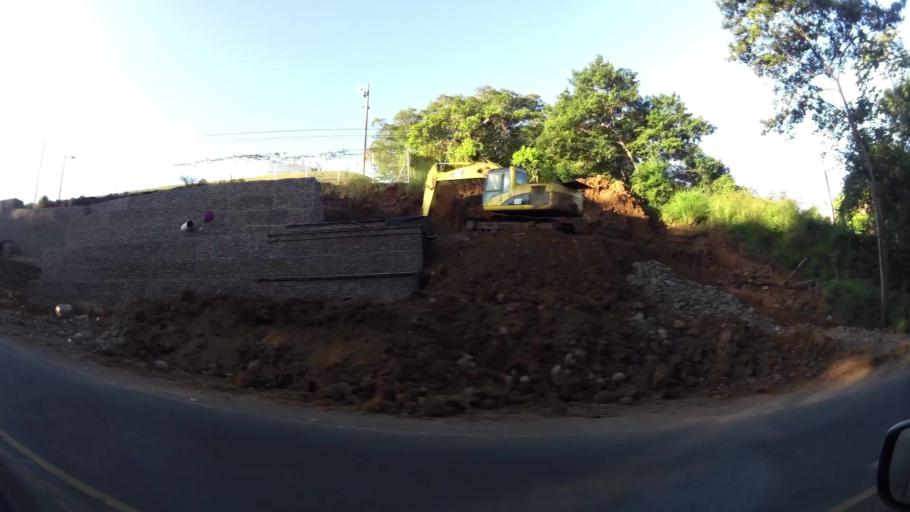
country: CR
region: Puntarenas
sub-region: Canton Central de Puntarenas
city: Chacarita
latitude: 10.0118
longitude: -84.7266
